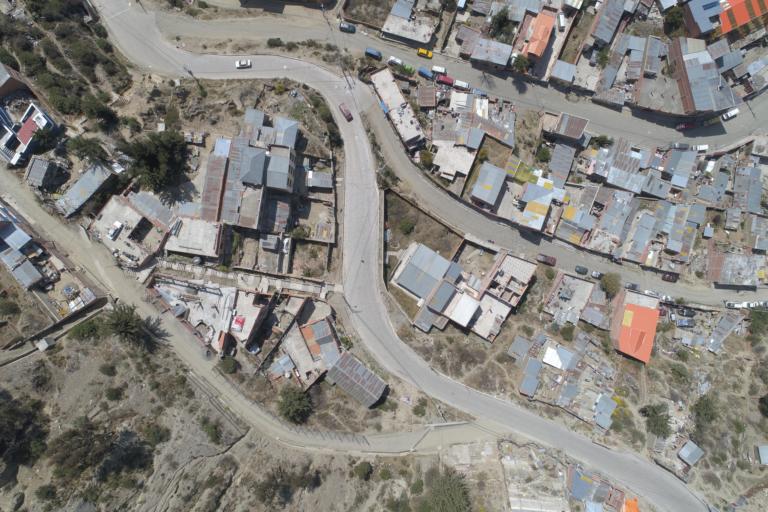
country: BO
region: La Paz
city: La Paz
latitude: -16.4977
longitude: -68.0986
